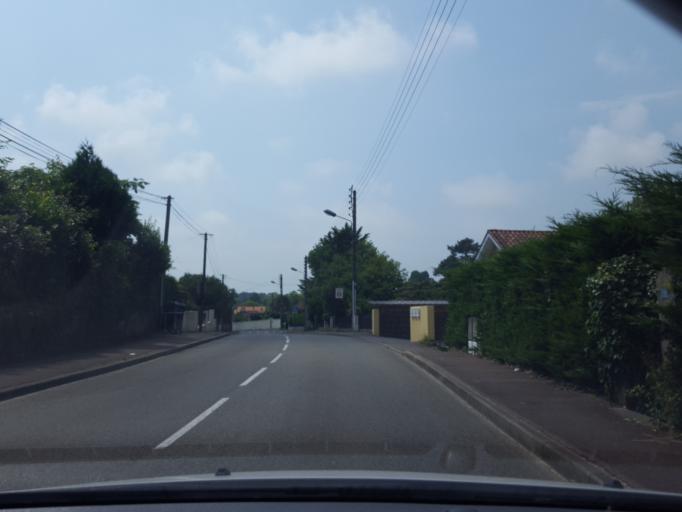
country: FR
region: Aquitaine
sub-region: Departement des Landes
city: Ondres
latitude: 43.5676
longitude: -1.4474
